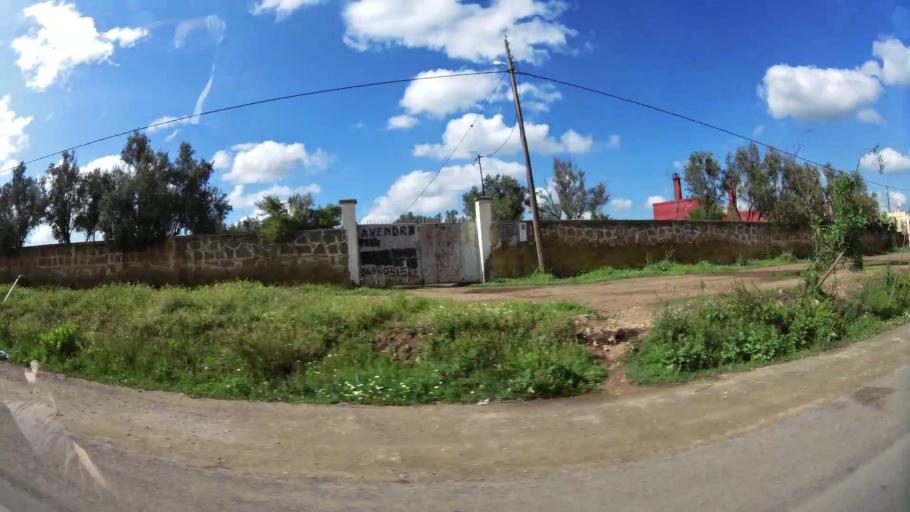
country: MA
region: Grand Casablanca
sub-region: Mediouna
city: Mediouna
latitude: 33.4100
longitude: -7.5372
